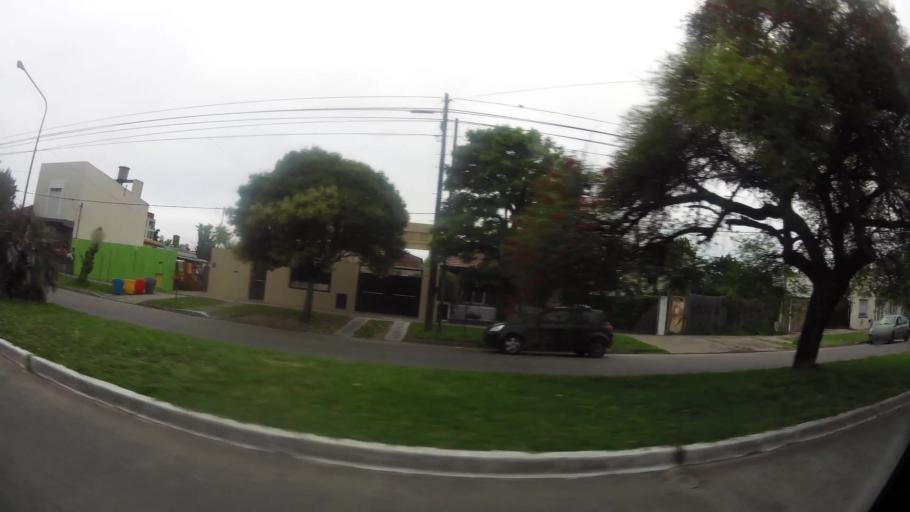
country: AR
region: Buenos Aires
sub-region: Partido de La Plata
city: La Plata
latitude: -34.9186
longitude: -57.9857
